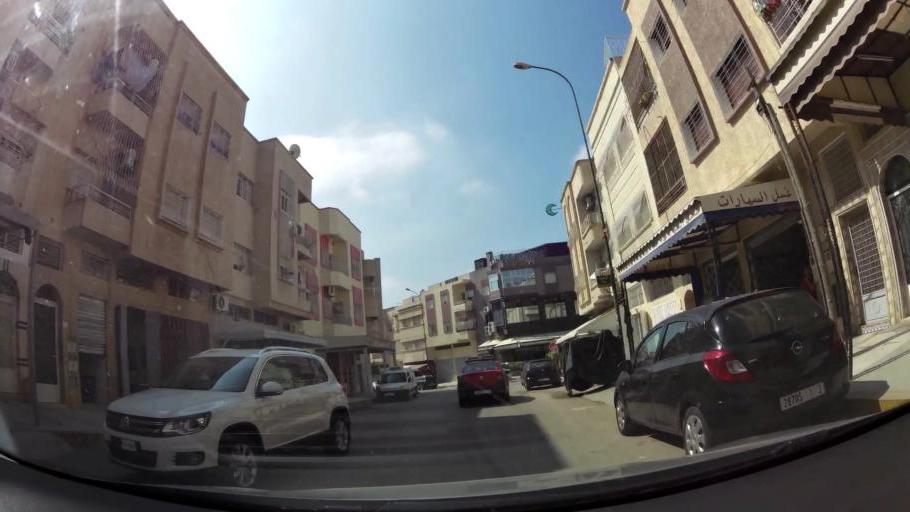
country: MA
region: Fes-Boulemane
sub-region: Fes
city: Fes
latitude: 34.0554
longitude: -5.0285
